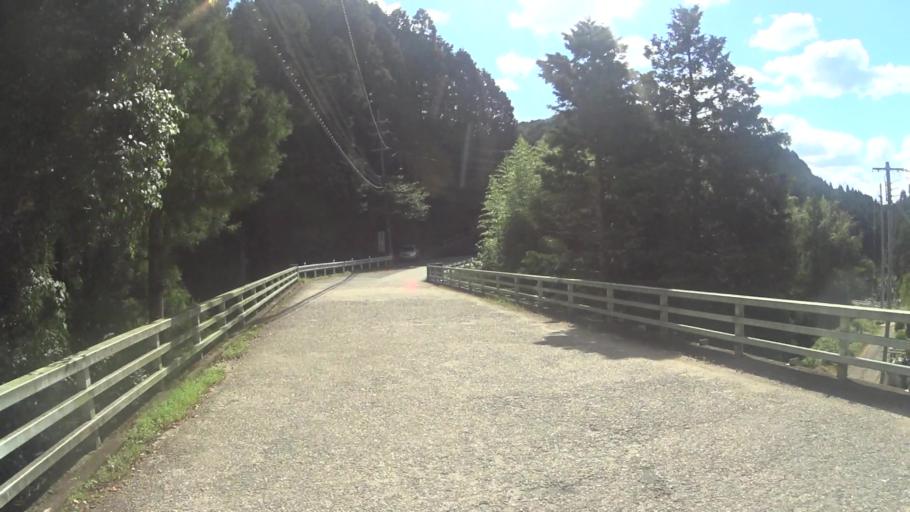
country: JP
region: Mie
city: Ueno-ebisumachi
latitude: 34.7706
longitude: 135.9963
